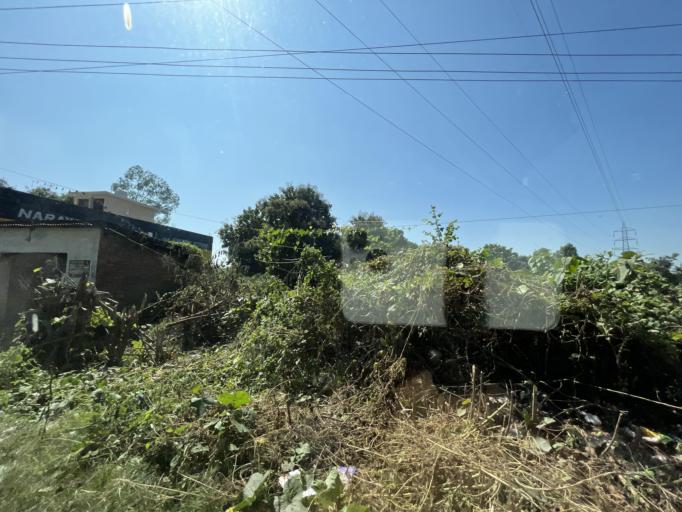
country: IN
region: Uttarakhand
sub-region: Naini Tal
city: Haldwani
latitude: 29.2112
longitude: 79.4617
